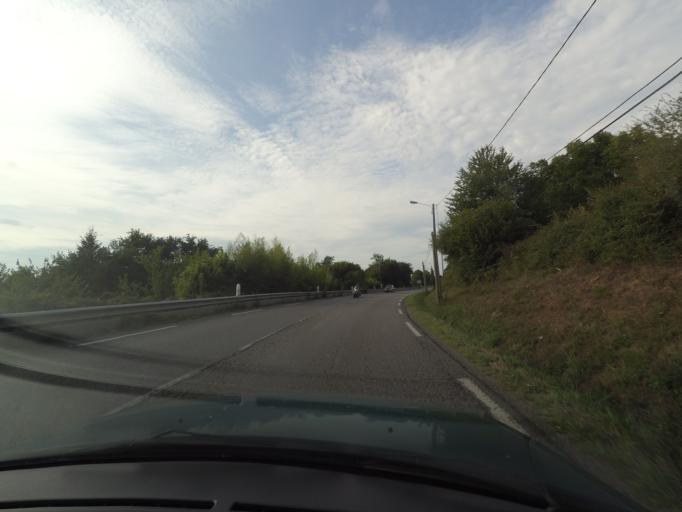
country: FR
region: Limousin
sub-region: Departement de la Haute-Vienne
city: Aixe-sur-Vienne
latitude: 45.7911
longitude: 1.1133
